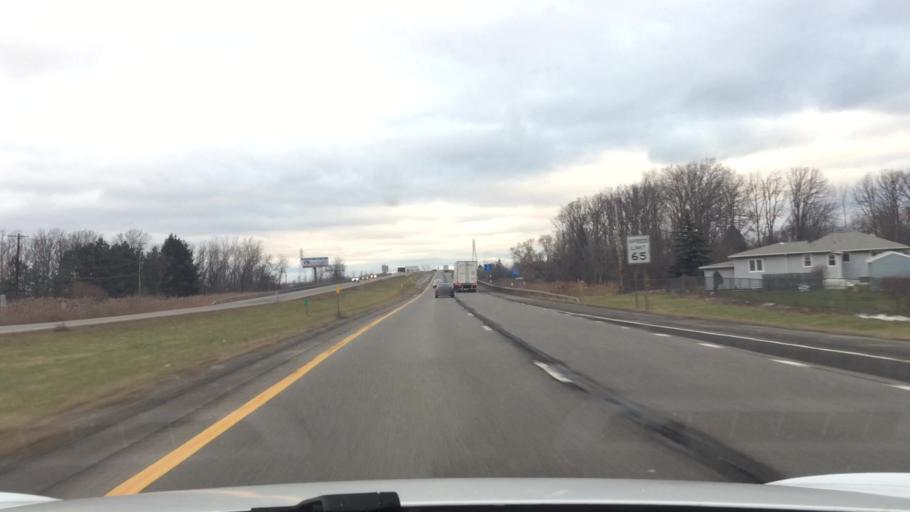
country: US
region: New York
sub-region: Niagara County
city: Niagara Falls
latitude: 43.1114
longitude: -78.9962
